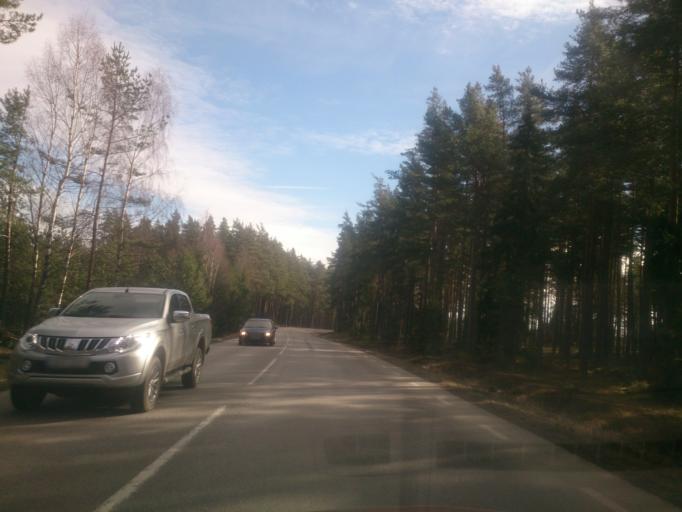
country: SE
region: OEstergoetland
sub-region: Finspangs Kommun
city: Finspang
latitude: 58.6641
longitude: 15.7742
